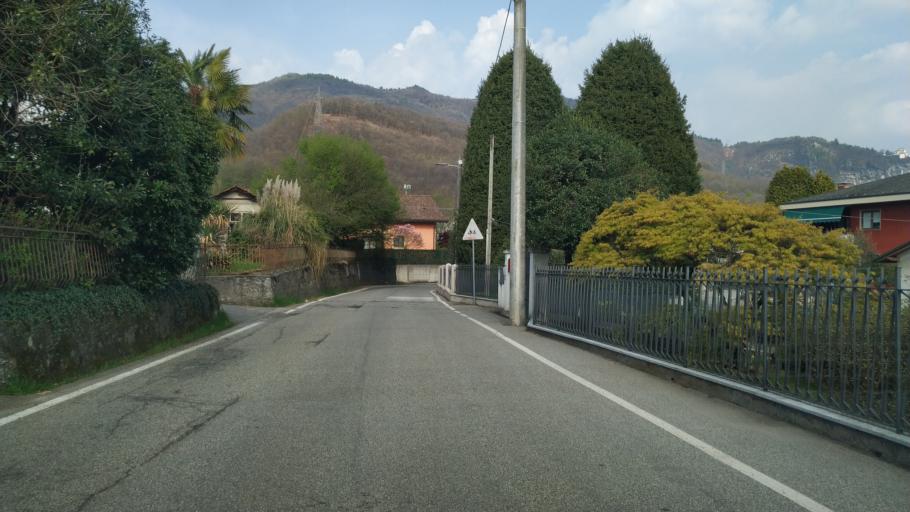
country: IT
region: Piedmont
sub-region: Provincia di Novara
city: San Maurizio D'Opaglio
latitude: 45.7721
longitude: 8.3903
